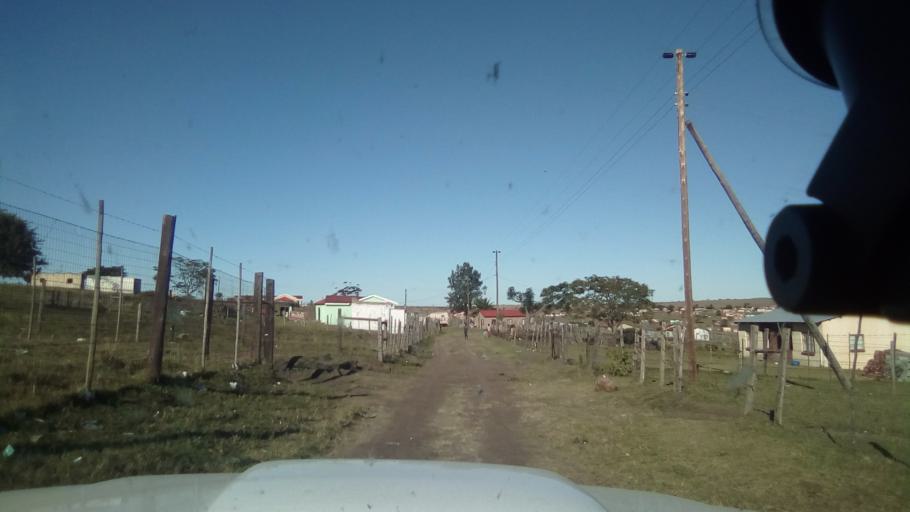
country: ZA
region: Eastern Cape
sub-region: Buffalo City Metropolitan Municipality
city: Bhisho
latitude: -32.9382
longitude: 27.2870
